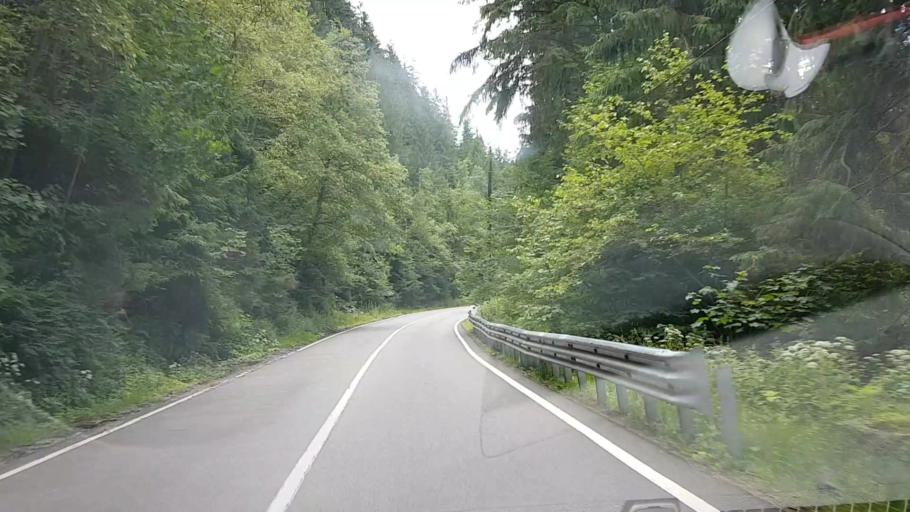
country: RO
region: Suceava
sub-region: Comuna Crucea
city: Crucea
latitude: 47.3643
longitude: 25.5918
